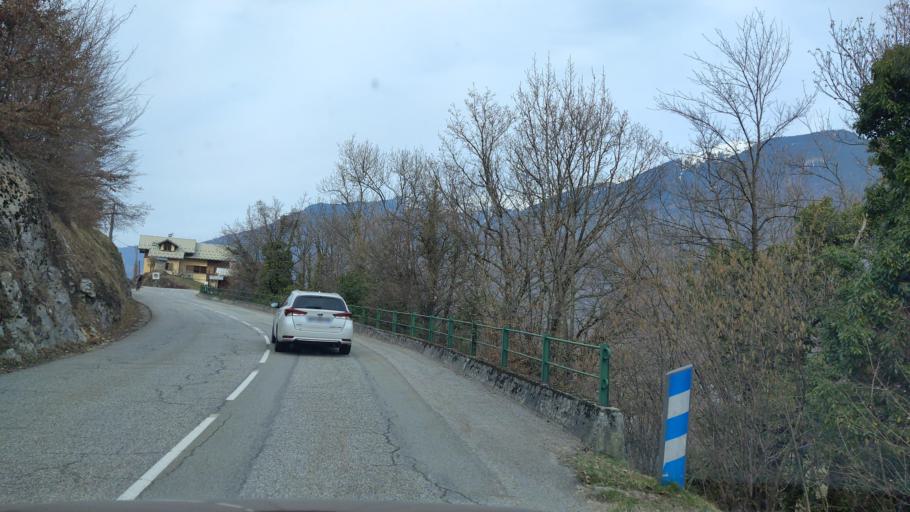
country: FR
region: Rhone-Alpes
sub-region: Departement de la Savoie
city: La Bathie
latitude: 45.6086
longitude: 6.4392
